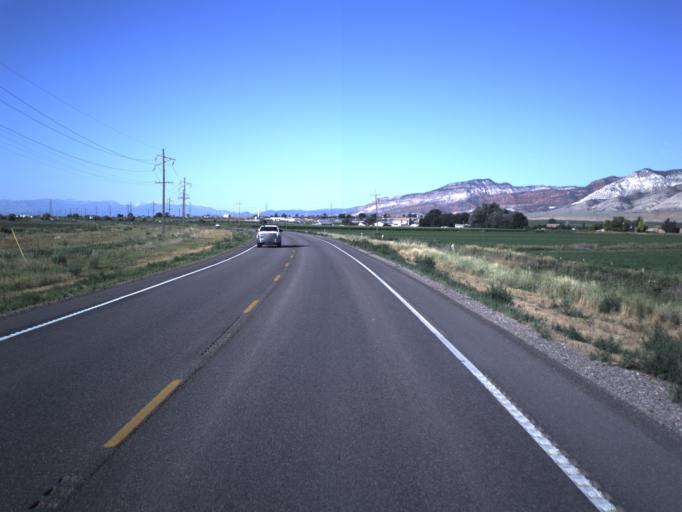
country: US
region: Utah
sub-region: Sevier County
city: Aurora
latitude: 38.9158
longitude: -111.9305
